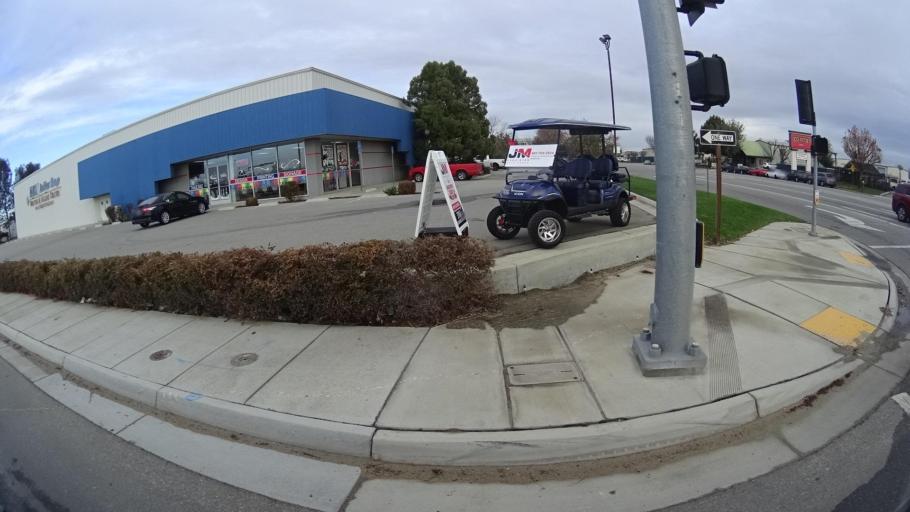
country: US
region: California
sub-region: Kern County
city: Bakersfield
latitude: 35.3835
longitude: -119.0593
